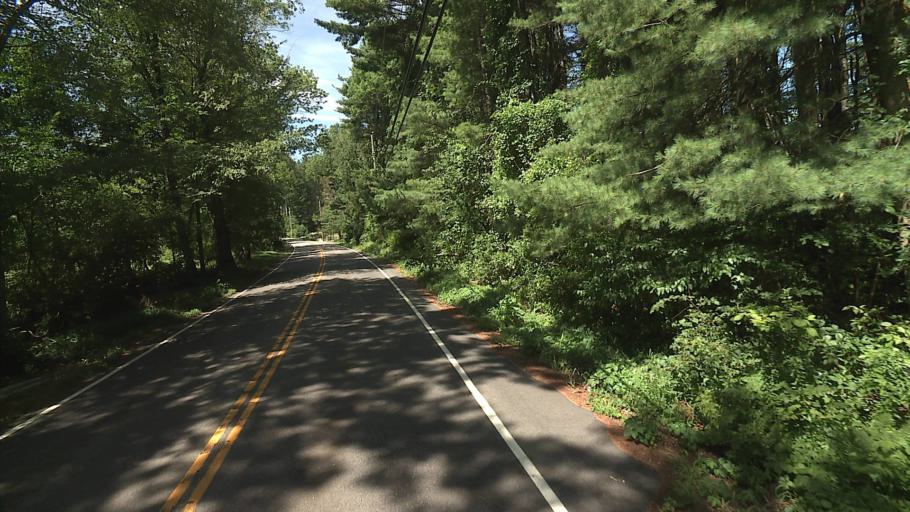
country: US
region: Connecticut
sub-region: Windham County
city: South Woodstock
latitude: 41.8993
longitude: -72.0133
